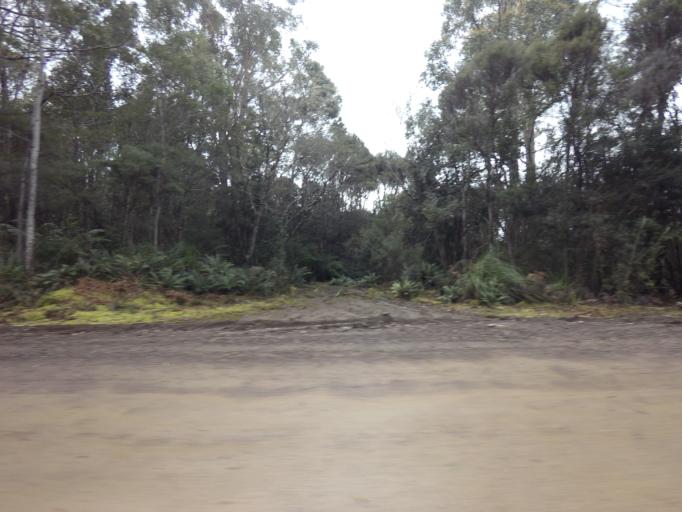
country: AU
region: Tasmania
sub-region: Huon Valley
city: Geeveston
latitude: -43.5537
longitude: 146.8845
